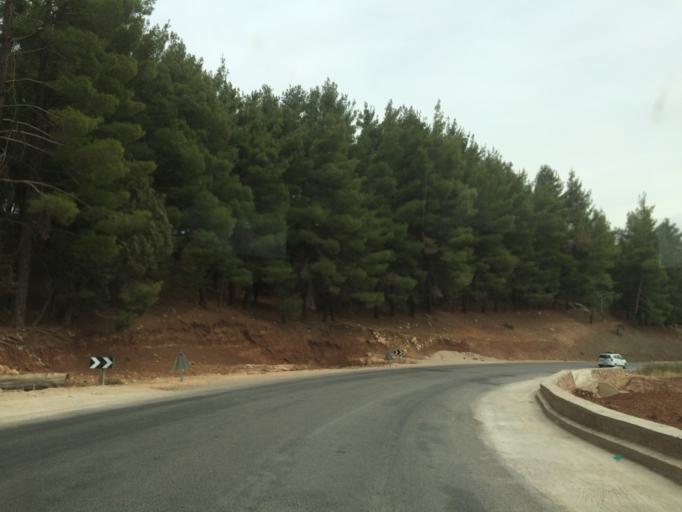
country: MA
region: Meknes-Tafilalet
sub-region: Ifrane
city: Azrou
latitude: 33.4976
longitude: -5.2672
